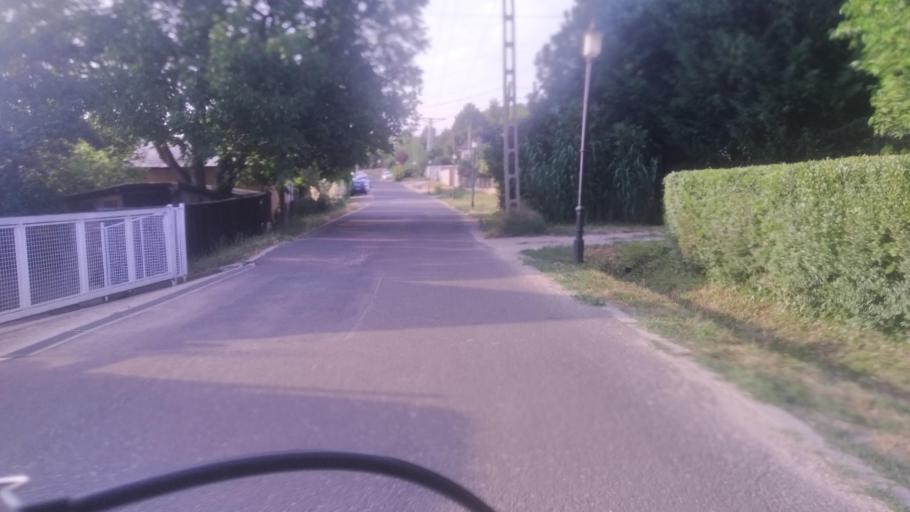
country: HU
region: Pest
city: Urom
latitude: 47.5938
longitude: 19.0214
